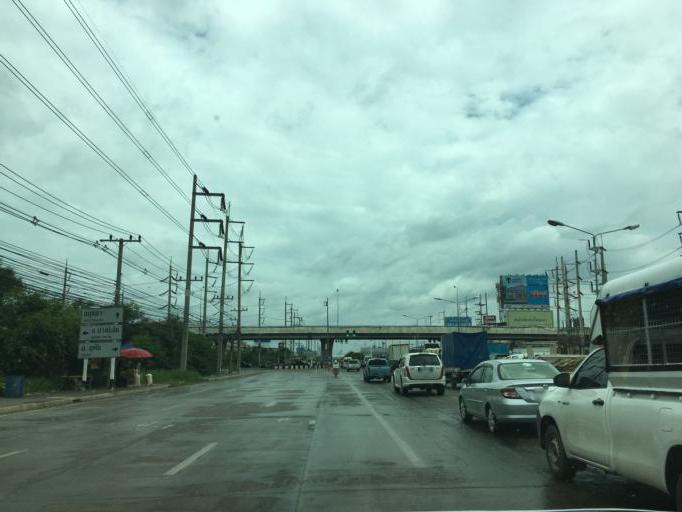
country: TH
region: Phra Nakhon Si Ayutthaya
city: Uthai
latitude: 14.3099
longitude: 100.6438
